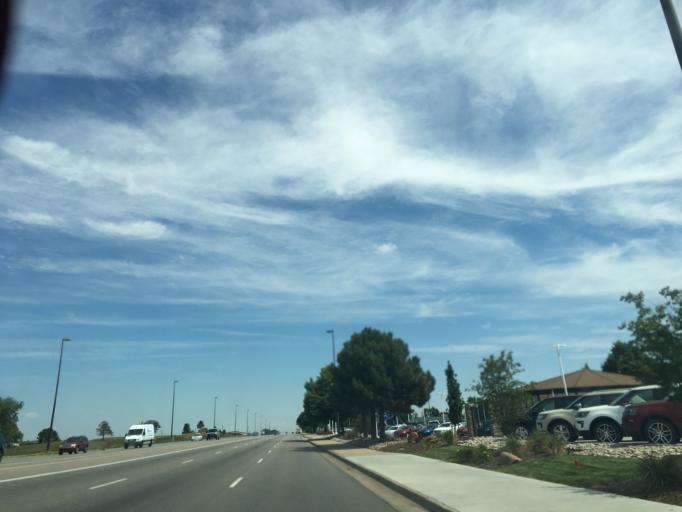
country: US
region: Colorado
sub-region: Adams County
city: Aurora
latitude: 39.7123
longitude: -104.8659
